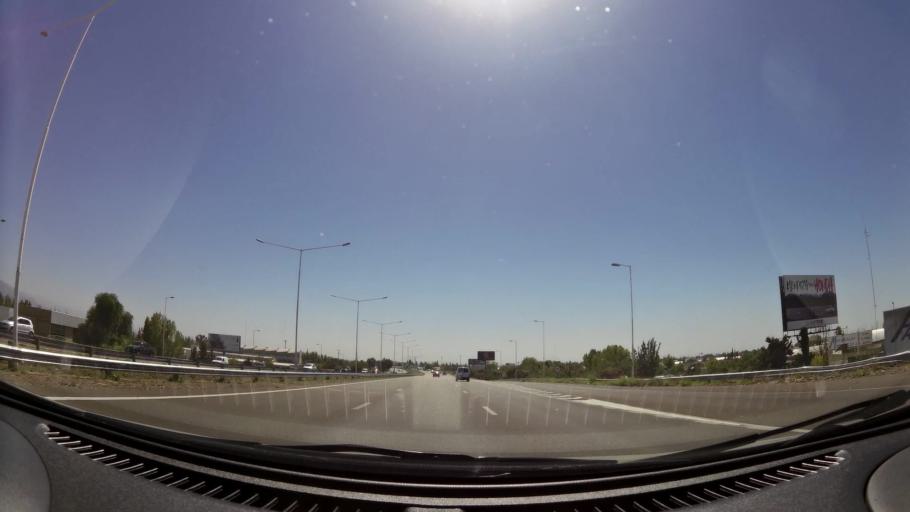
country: AR
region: Mendoza
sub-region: Departamento de Godoy Cruz
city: Godoy Cruz
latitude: -32.9309
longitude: -68.8264
